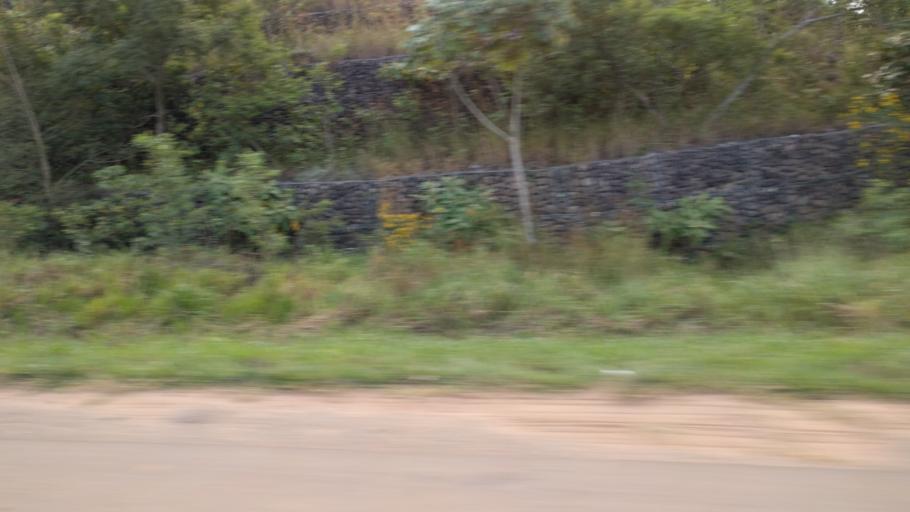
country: BO
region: Santa Cruz
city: Buena Vista
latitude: -17.4391
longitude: -63.6428
